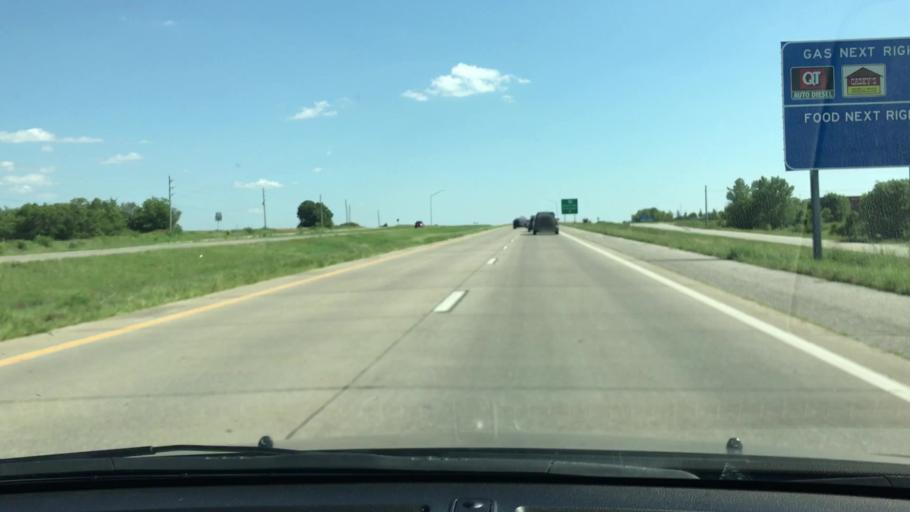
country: US
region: Missouri
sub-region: Jackson County
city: Greenwood
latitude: 38.8603
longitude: -94.3755
